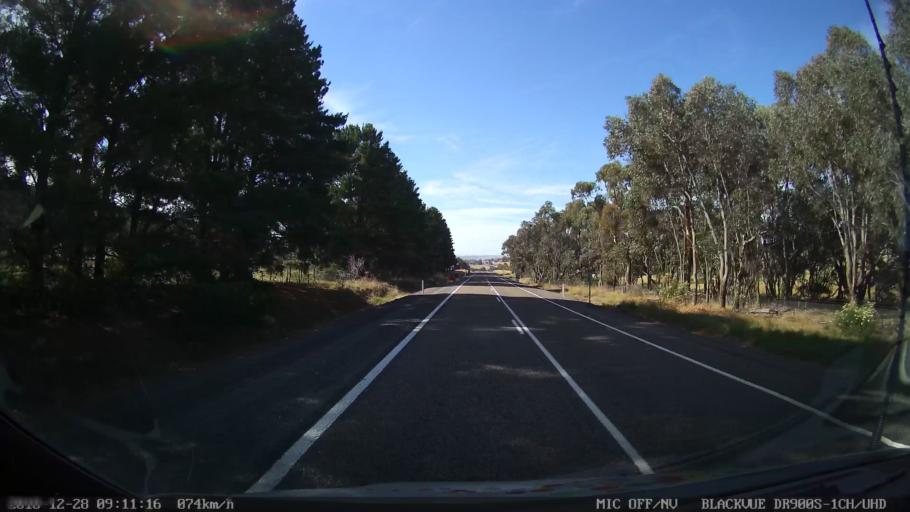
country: AU
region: New South Wales
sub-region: Upper Lachlan Shire
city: Crookwell
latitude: -34.2416
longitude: 149.3385
